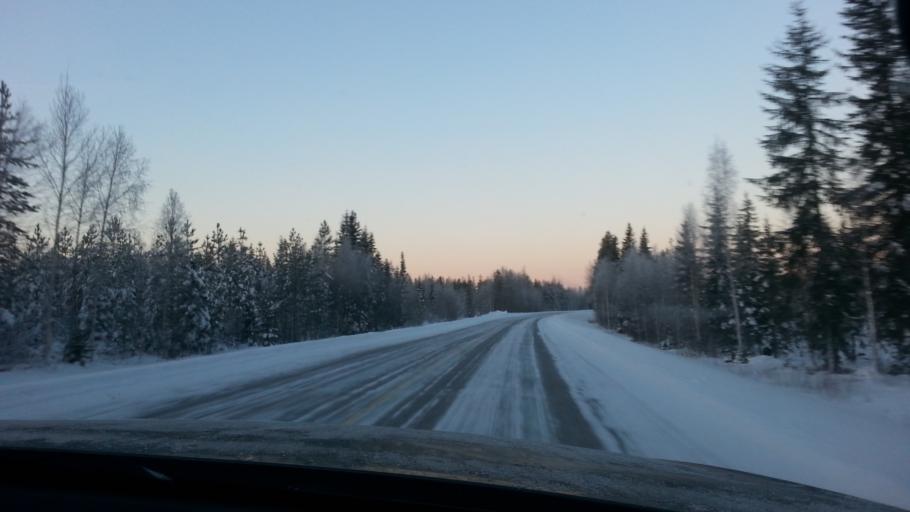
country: FI
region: Lapland
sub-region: Rovaniemi
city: Rovaniemi
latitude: 66.7789
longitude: 25.4500
